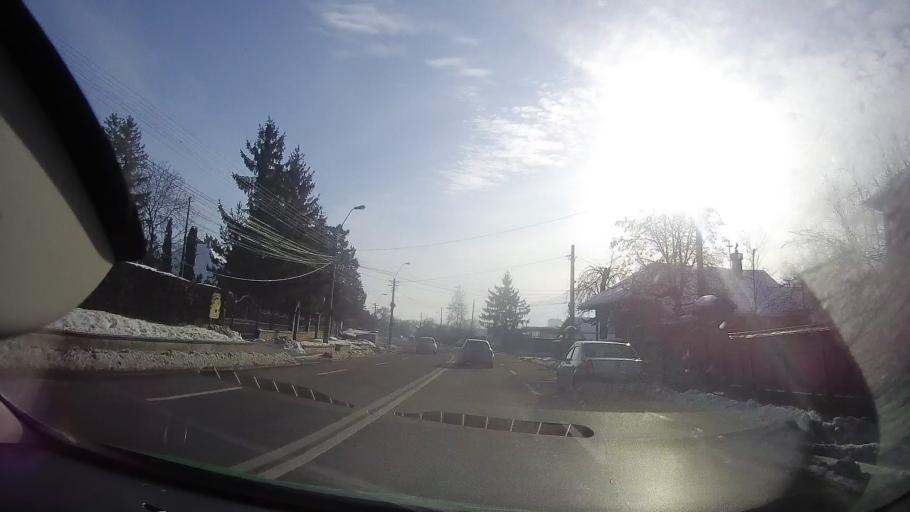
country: RO
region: Neamt
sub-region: Municipiul Piatra-Neamt
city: Valeni
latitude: 46.9490
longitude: 26.3846
